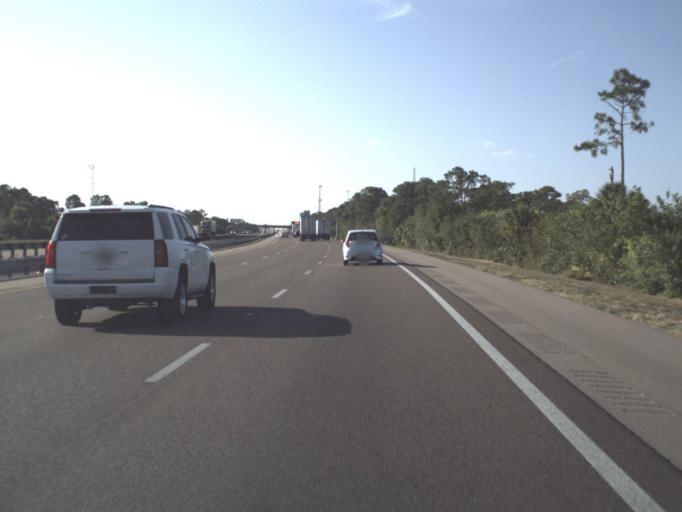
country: US
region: Florida
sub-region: Brevard County
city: Malabar
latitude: 27.9792
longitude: -80.6167
